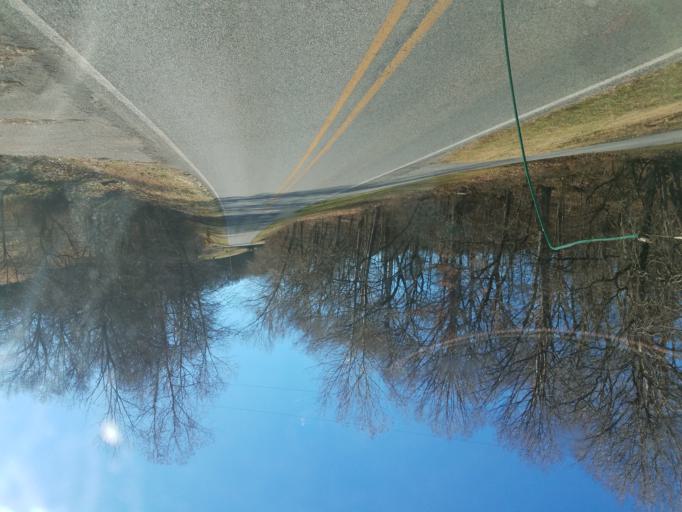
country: US
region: Arkansas
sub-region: Washington County
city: Elkins
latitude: 36.0314
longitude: -93.9419
